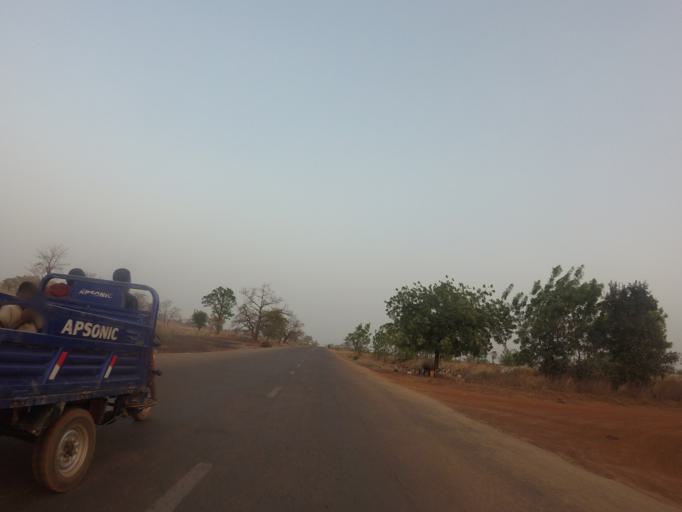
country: GH
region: Northern
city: Tamale
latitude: 9.4399
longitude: -1.0990
